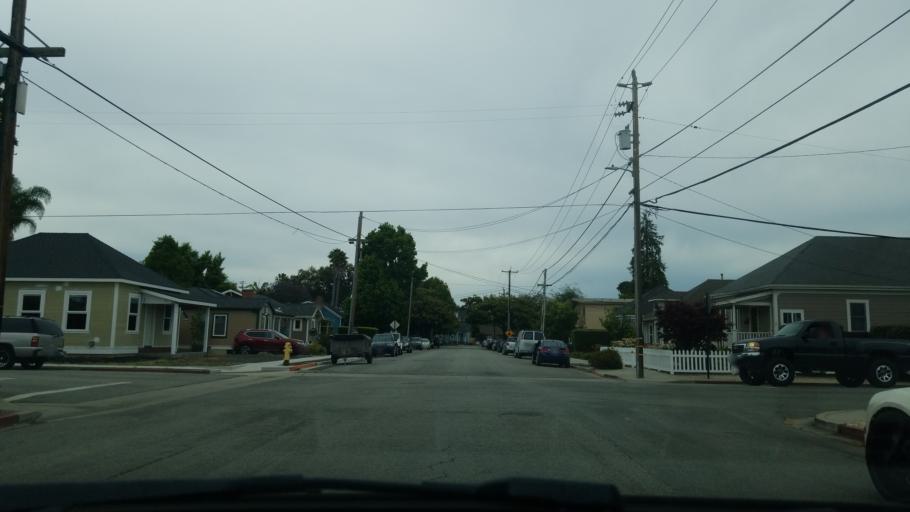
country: US
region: California
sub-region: San Luis Obispo County
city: Arroyo Grande
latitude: 35.1220
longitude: -120.5747
